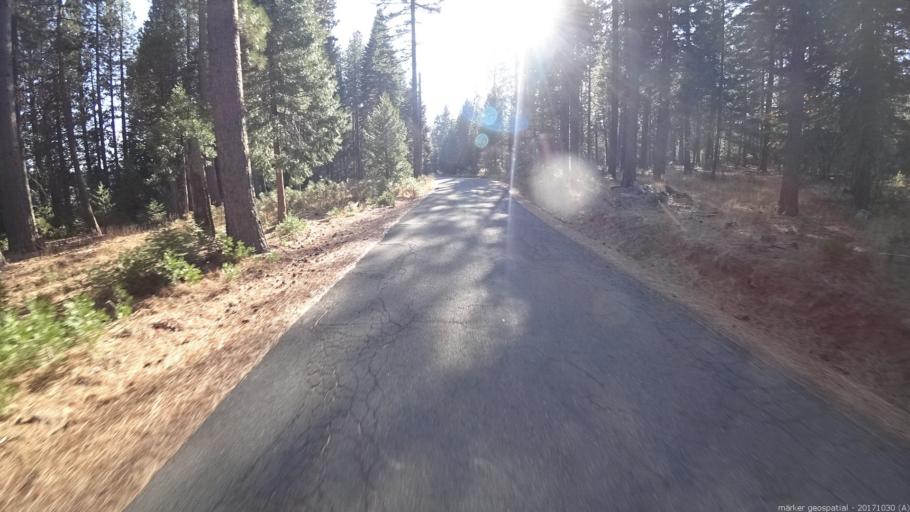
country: US
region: California
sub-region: Shasta County
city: Shingletown
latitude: 40.5445
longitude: -121.7346
